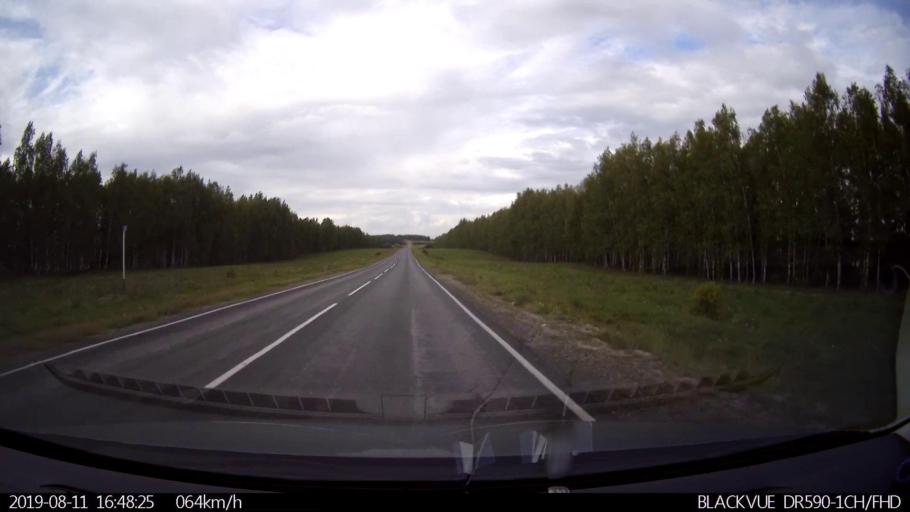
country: RU
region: Ulyanovsk
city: Mayna
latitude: 54.2089
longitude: 47.6922
